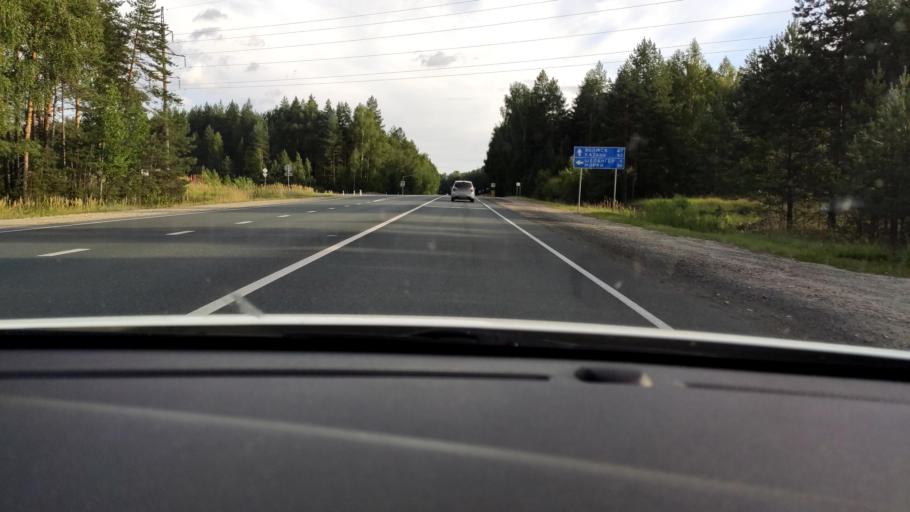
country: RU
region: Mariy-El
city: Suslonger
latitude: 56.2425
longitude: 48.2320
